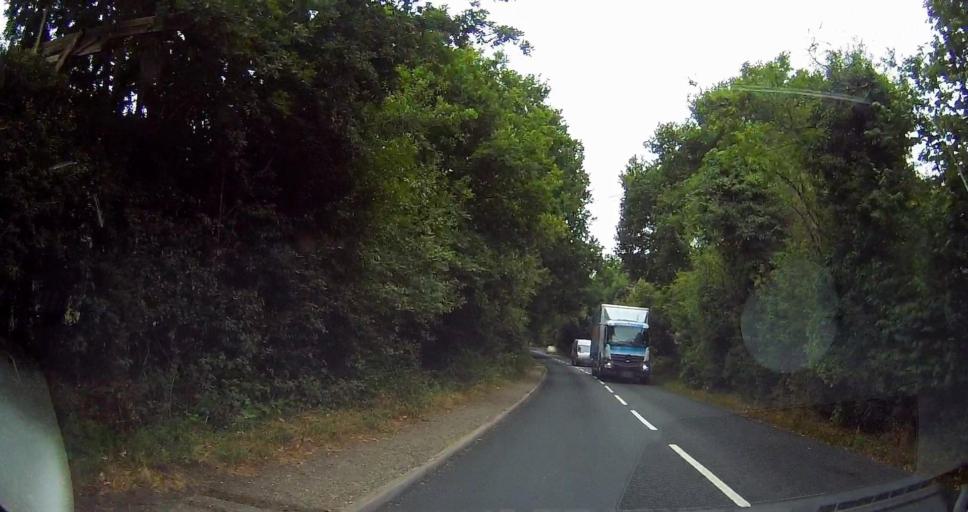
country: GB
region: England
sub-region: East Sussex
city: Wadhurst
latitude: 51.0938
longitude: 0.3912
